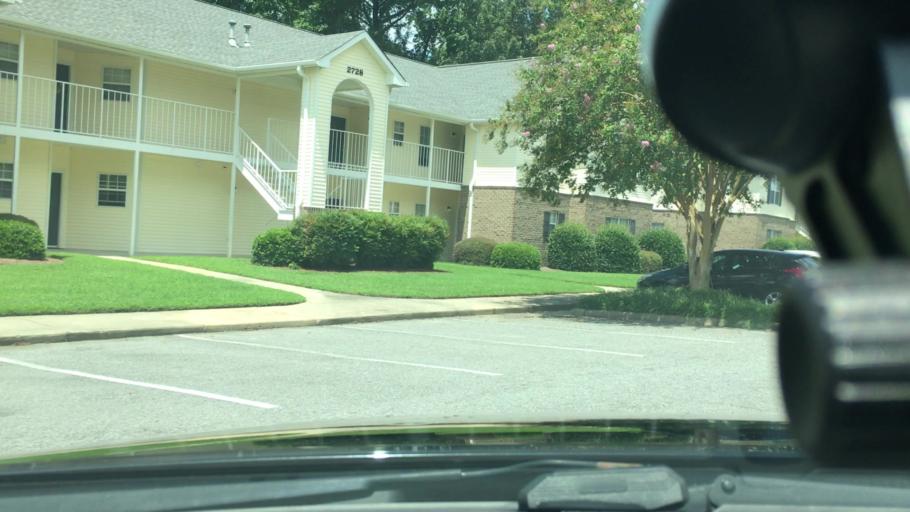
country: US
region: North Carolina
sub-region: Pitt County
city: Summerfield
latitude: 35.5892
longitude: -77.3996
